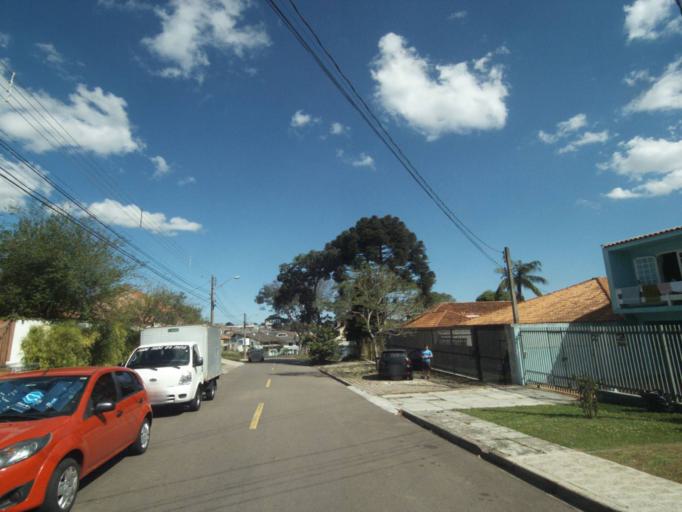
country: BR
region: Parana
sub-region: Curitiba
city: Curitiba
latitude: -25.3842
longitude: -49.2595
